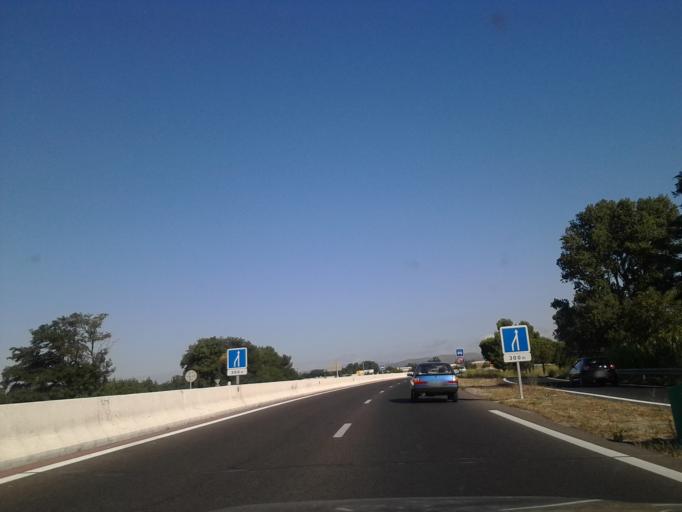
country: FR
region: Languedoc-Roussillon
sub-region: Departement des Pyrenees-Orientales
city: Perpignan
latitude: 42.7092
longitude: 2.8770
